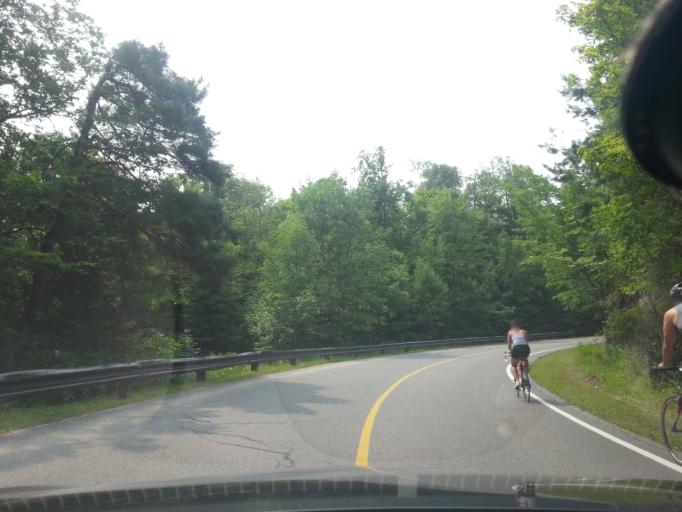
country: CA
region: Quebec
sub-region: Outaouais
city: Wakefield
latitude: 45.5205
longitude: -75.8504
